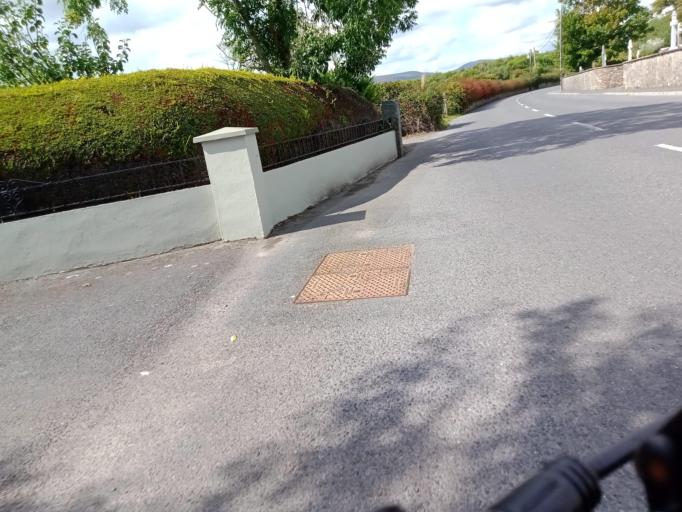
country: IE
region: Munster
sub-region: Waterford
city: Dungarvan
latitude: 52.1358
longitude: -7.4679
